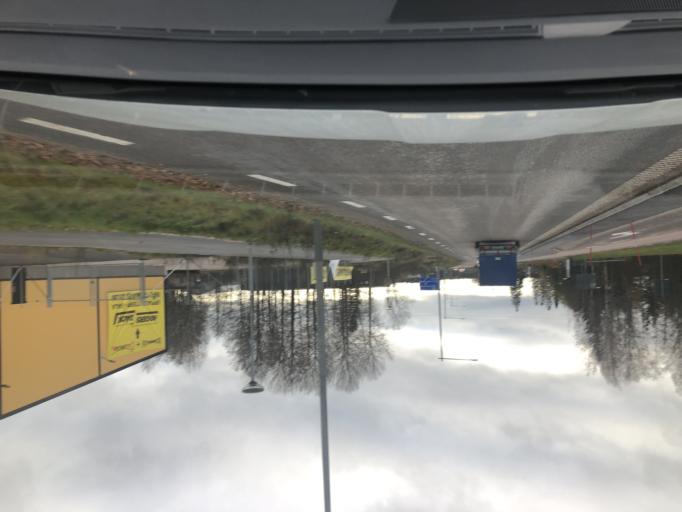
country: SE
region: Uppsala
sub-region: Tierps Kommun
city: Tierp
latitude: 60.3485
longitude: 17.4975
